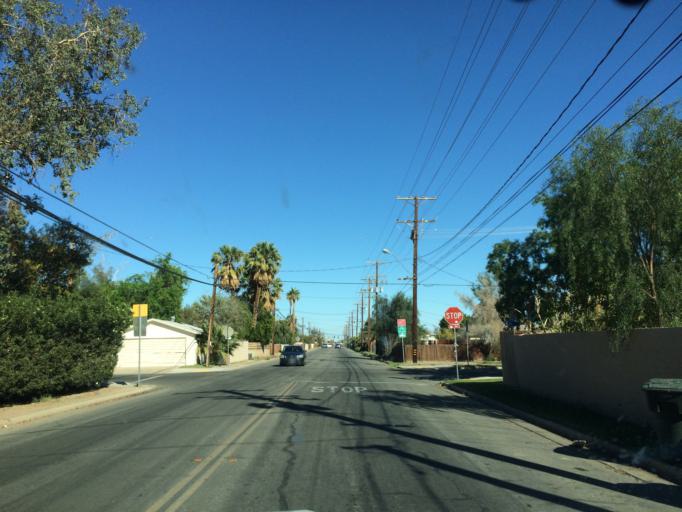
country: US
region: California
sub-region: Imperial County
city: El Centro
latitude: 32.7815
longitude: -115.5573
